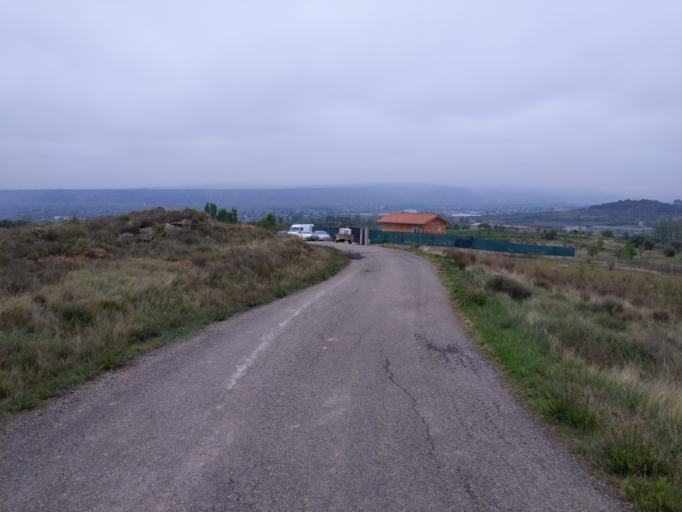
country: ES
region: La Rioja
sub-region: Provincia de La Rioja
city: Lardero
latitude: 42.4084
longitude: -2.4874
